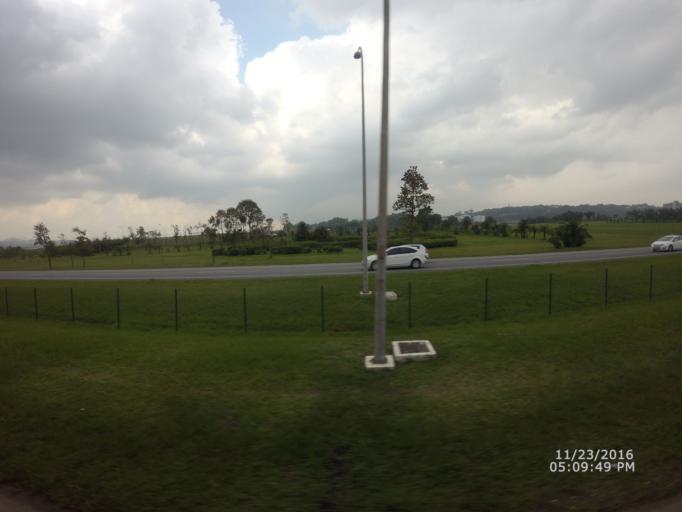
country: BR
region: Sao Paulo
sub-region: Guarulhos
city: Guarulhos
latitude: -23.4425
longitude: -46.4949
